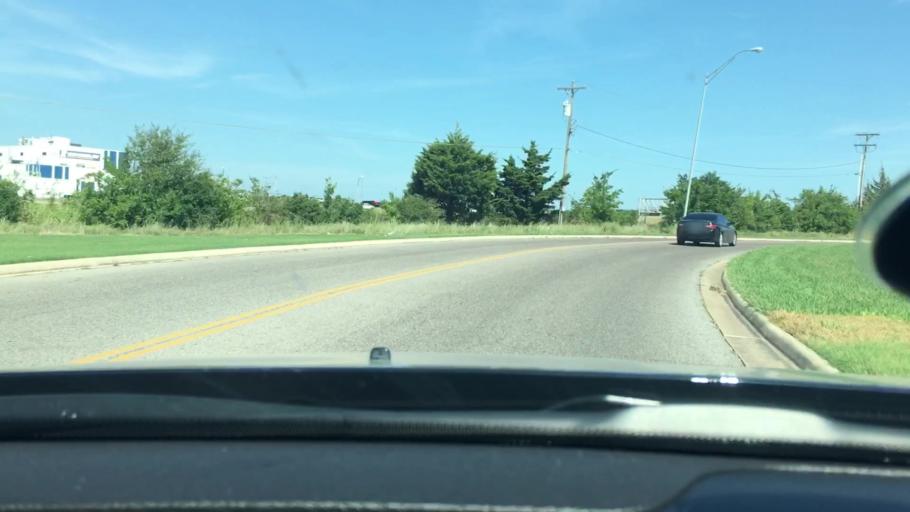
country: US
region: Oklahoma
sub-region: Carter County
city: Ardmore
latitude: 34.1810
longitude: -97.1666
